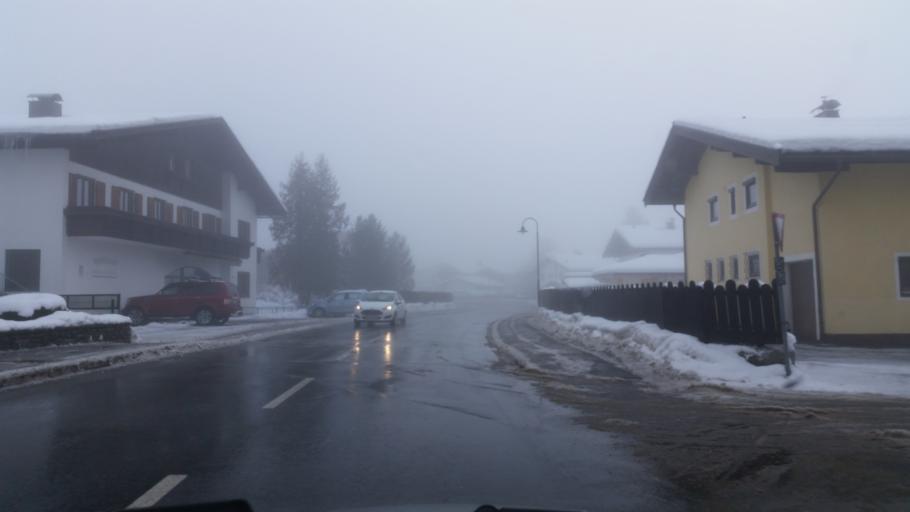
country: AT
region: Tyrol
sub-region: Politischer Bezirk Kitzbuhel
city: Kirchdorf in Tirol
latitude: 47.5555
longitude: 12.4509
